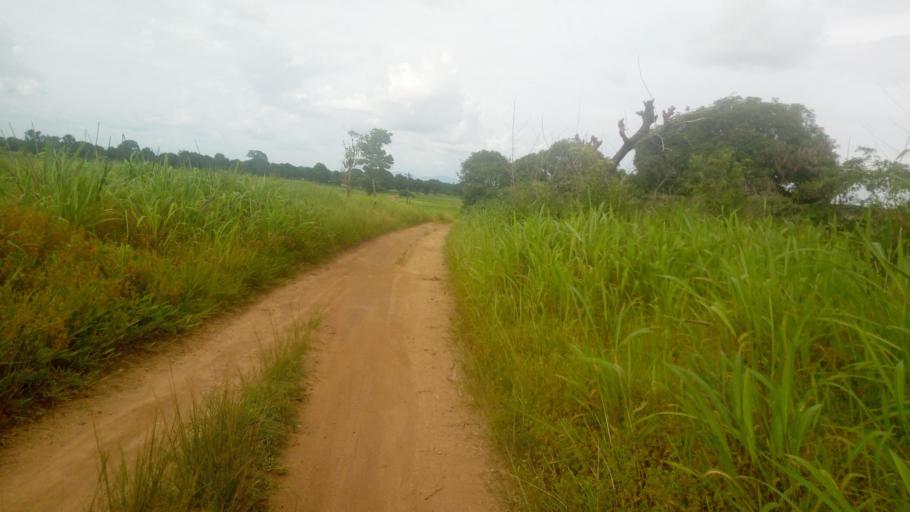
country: SL
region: Northern Province
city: Magburaka
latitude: 8.6741
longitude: -12.0170
